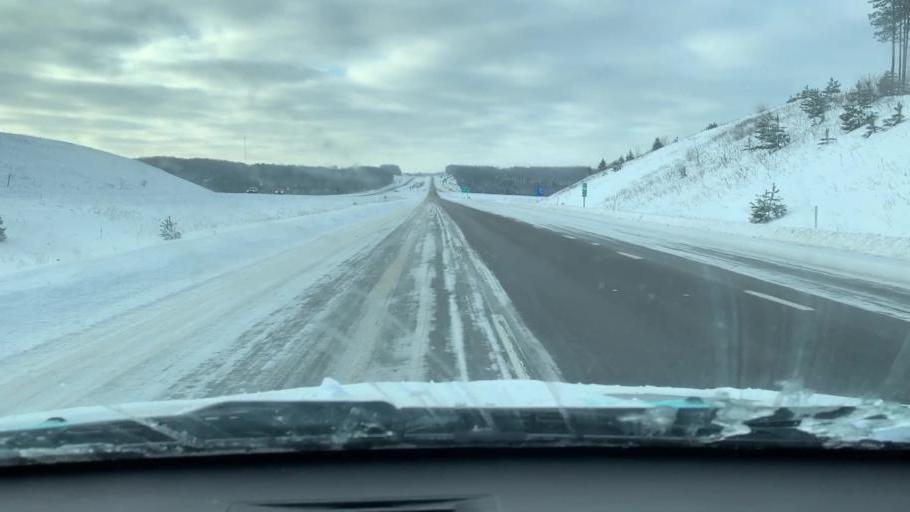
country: US
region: Michigan
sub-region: Wexford County
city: Manton
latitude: 44.4104
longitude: -85.3811
